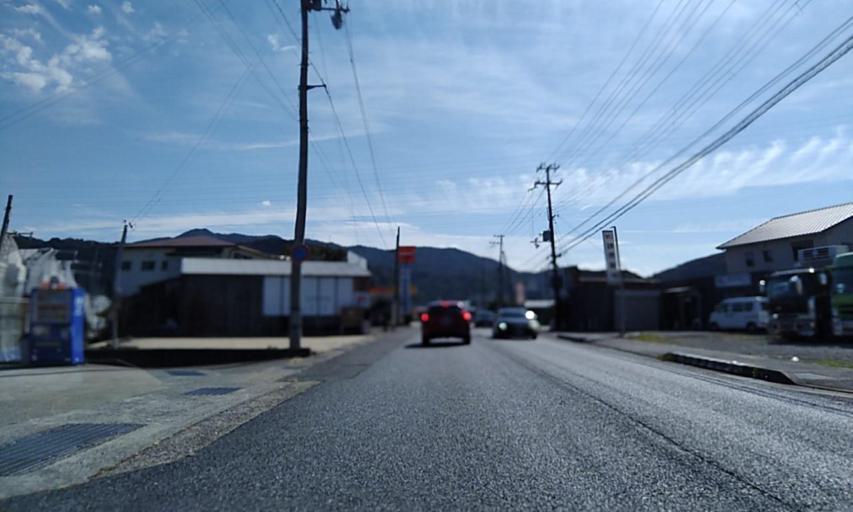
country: JP
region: Wakayama
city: Kainan
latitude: 34.0201
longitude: 135.1806
